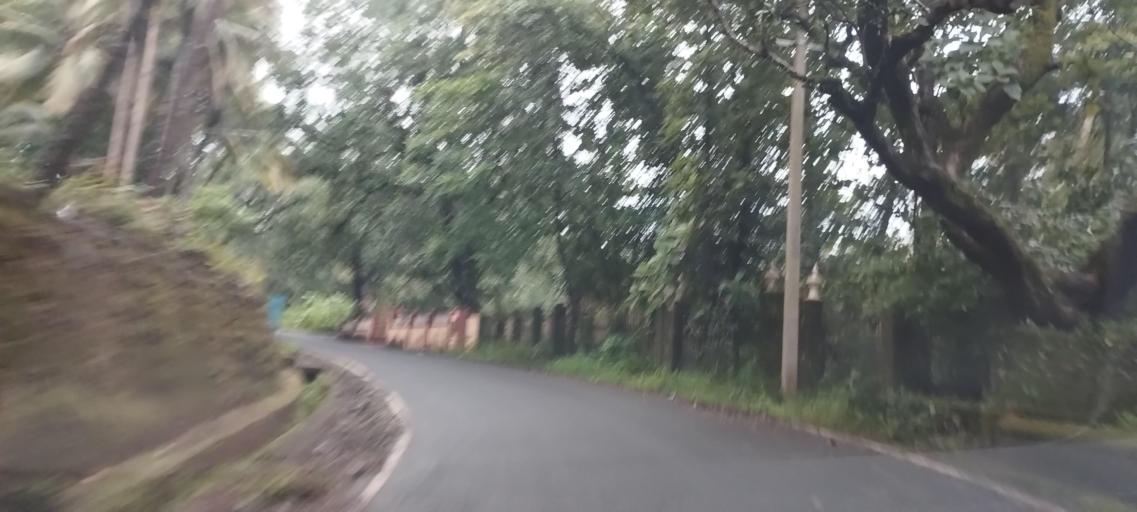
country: IN
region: Goa
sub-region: North Goa
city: Jua
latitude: 15.5213
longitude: 73.8971
